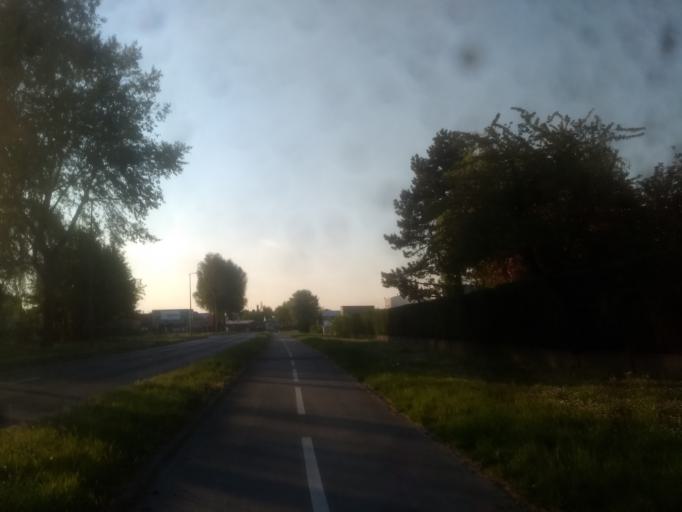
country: FR
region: Nord-Pas-de-Calais
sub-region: Departement du Pas-de-Calais
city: Saint-Laurent-Blangy
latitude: 50.2866
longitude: 2.8101
